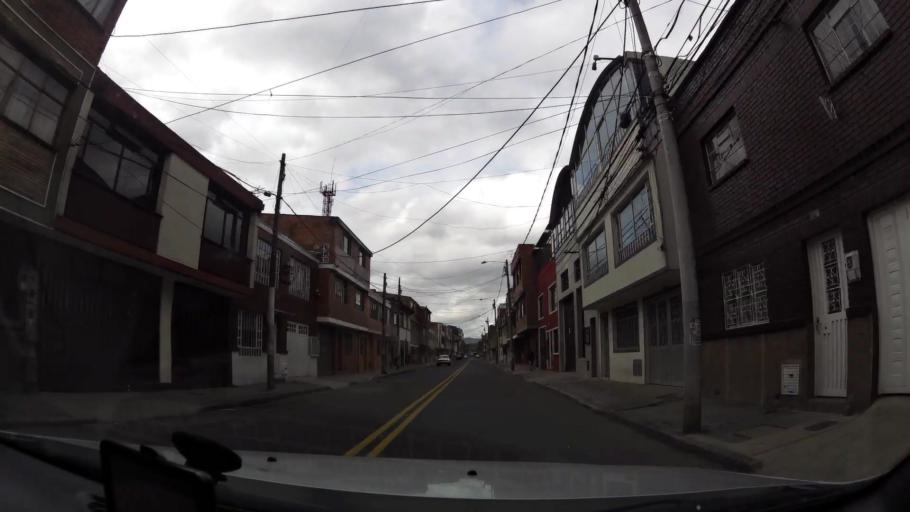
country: CO
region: Bogota D.C.
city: Bogota
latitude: 4.6263
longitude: -74.1159
